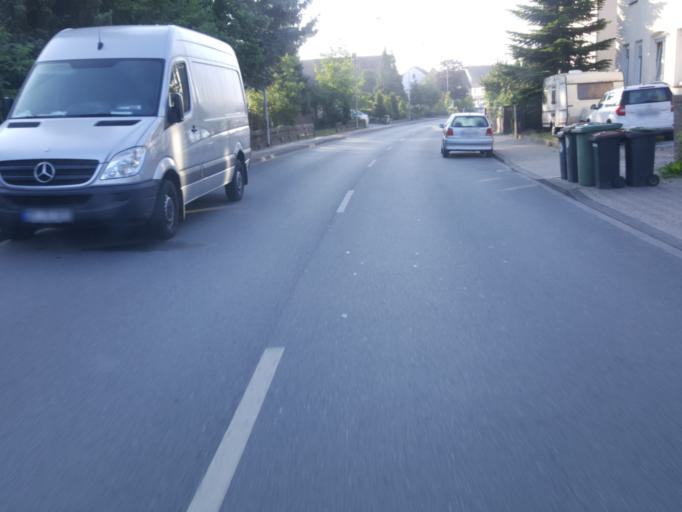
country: DE
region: North Rhine-Westphalia
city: Buende
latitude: 52.2000
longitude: 8.5952
